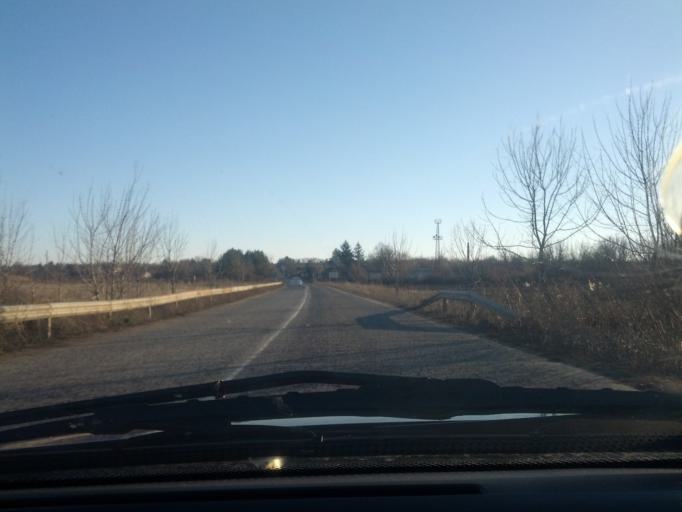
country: BG
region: Vratsa
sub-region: Obshtina Borovan
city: Borovan
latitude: 43.5403
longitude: 23.7979
